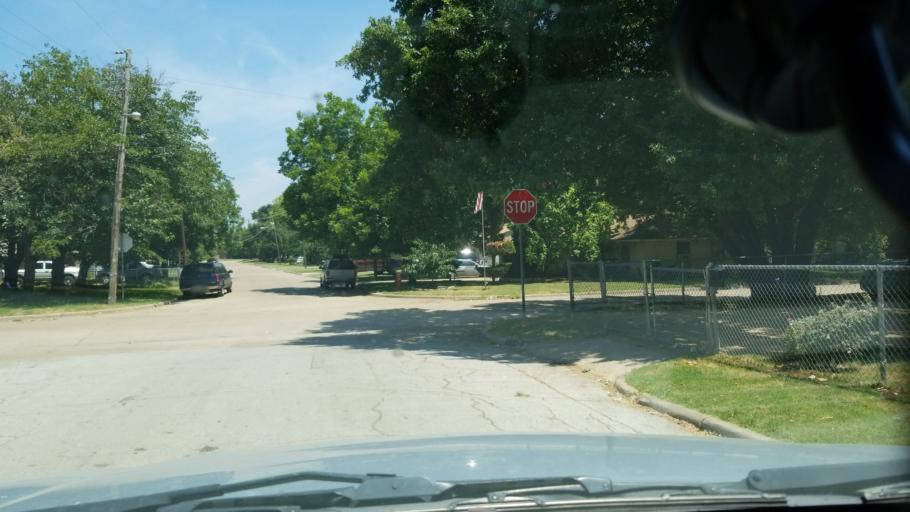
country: US
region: Texas
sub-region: Dallas County
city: Grand Prairie
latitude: 32.7579
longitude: -96.9569
